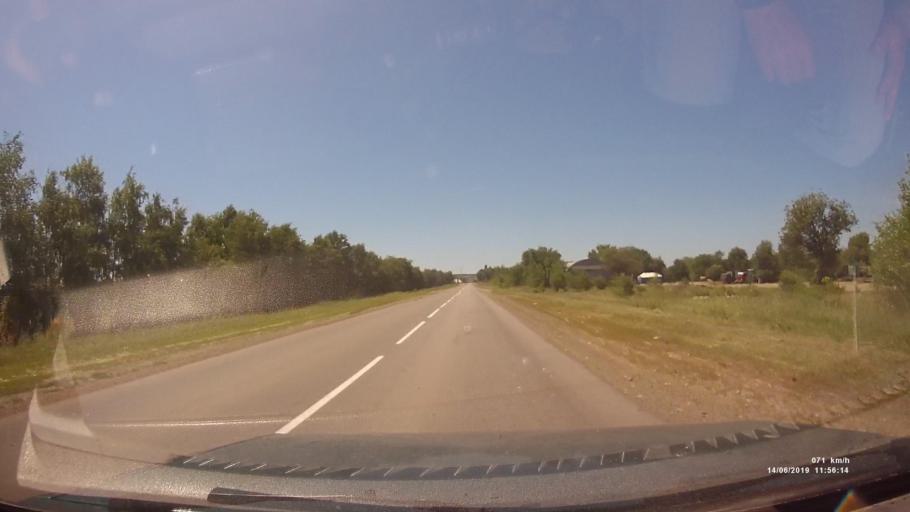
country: RU
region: Rostov
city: Kazanskaya
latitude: 49.8043
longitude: 41.1641
